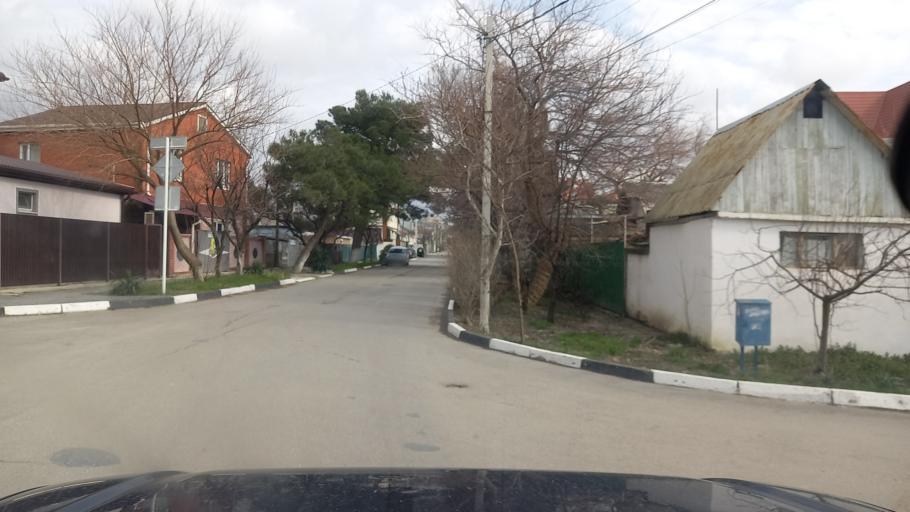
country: RU
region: Krasnodarskiy
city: Gelendzhik
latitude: 44.5589
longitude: 38.0885
